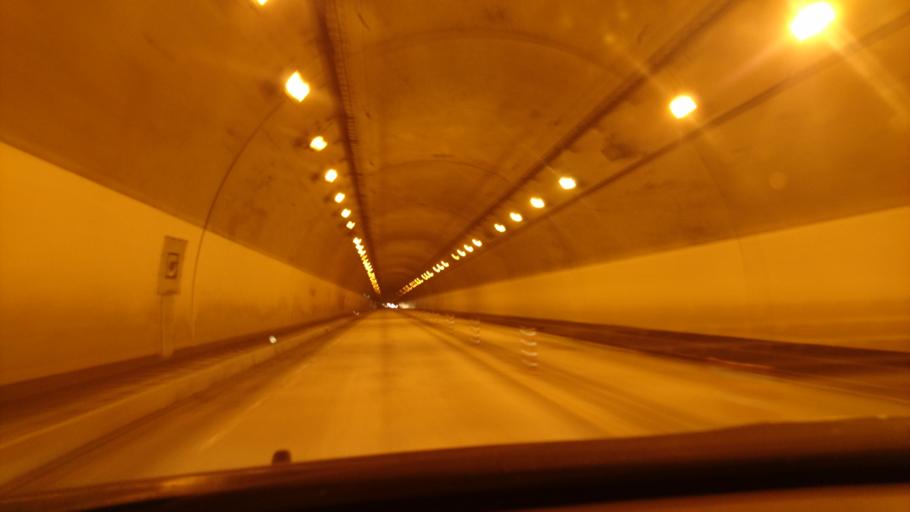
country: JP
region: Iwate
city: Ofunato
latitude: 38.9331
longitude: 141.6178
